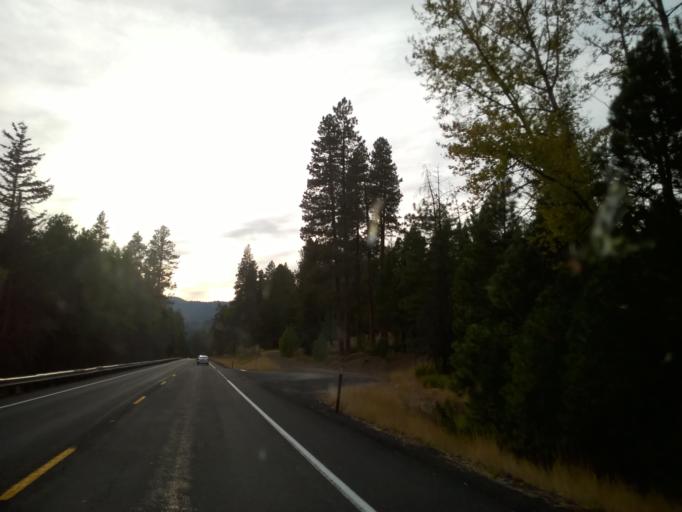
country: US
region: Washington
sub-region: Chelan County
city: Cashmere
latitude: 47.3300
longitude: -120.6496
